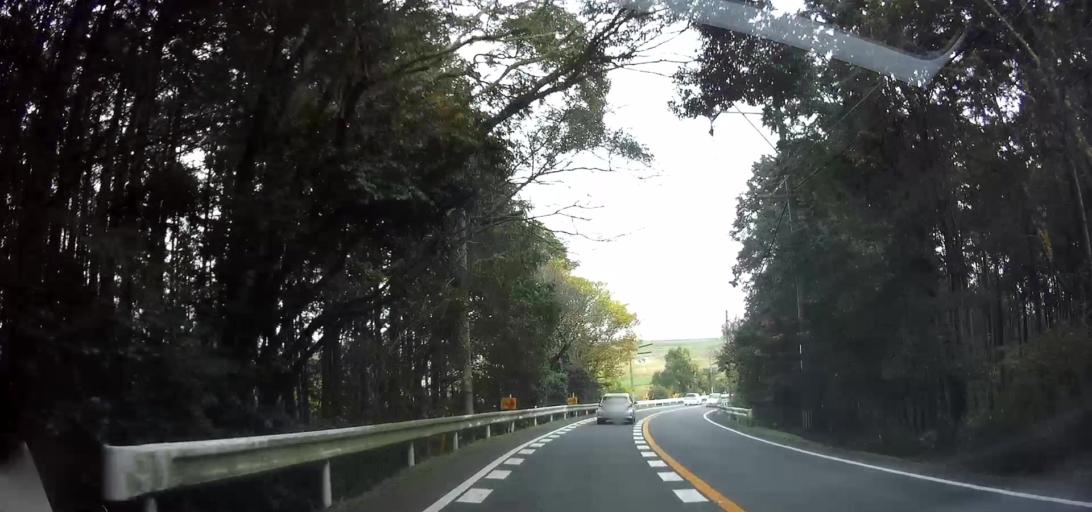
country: JP
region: Nagasaki
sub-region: Isahaya-shi
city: Isahaya
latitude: 32.7887
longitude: 130.0462
